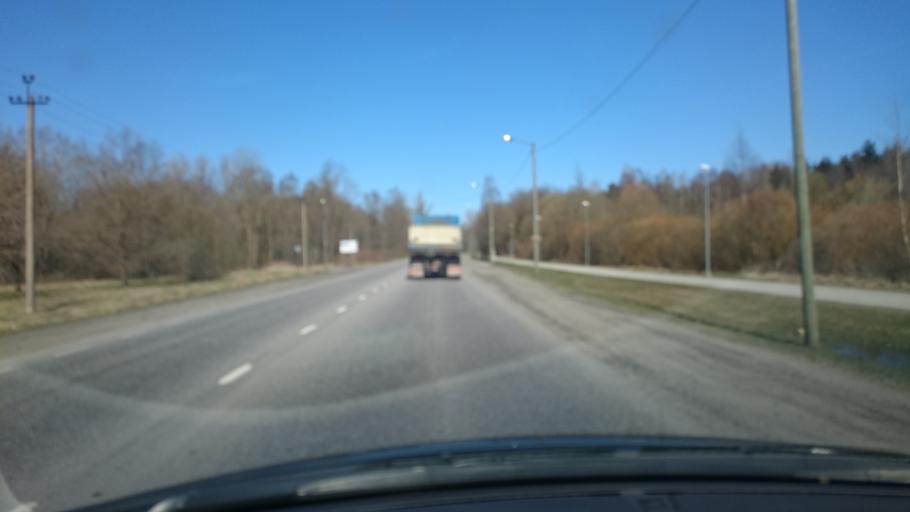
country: EE
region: Harju
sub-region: Tallinna linn
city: Kose
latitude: 59.4638
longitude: 24.9038
